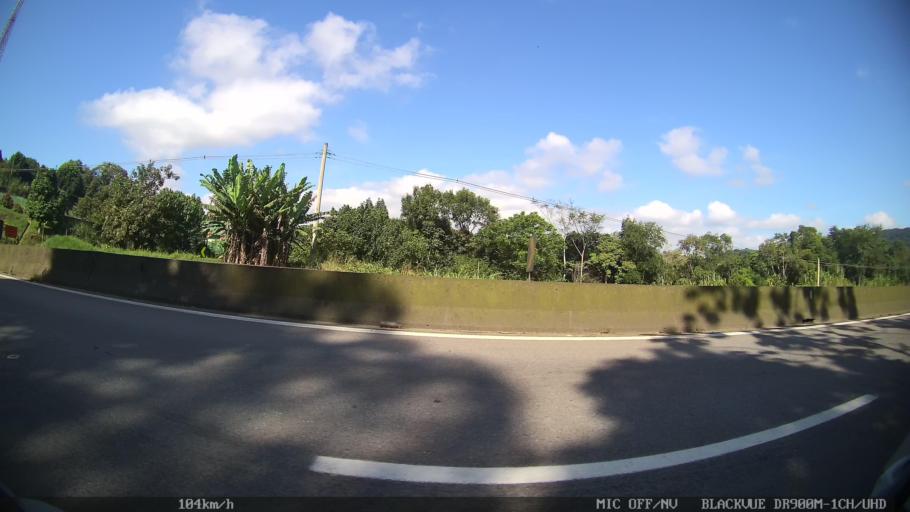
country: BR
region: Sao Paulo
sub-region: Miracatu
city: Miracatu
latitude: -24.1452
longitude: -47.2754
